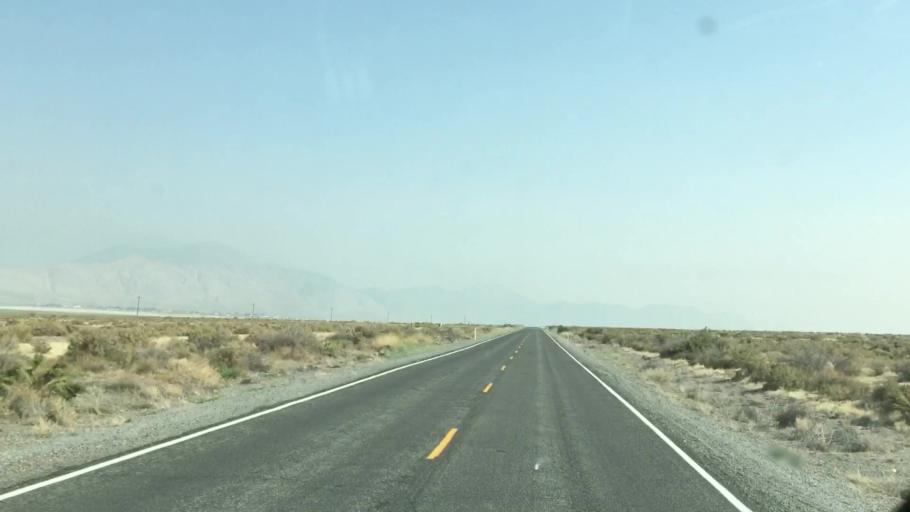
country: US
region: Nevada
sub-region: Pershing County
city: Lovelock
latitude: 40.6107
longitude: -119.3348
